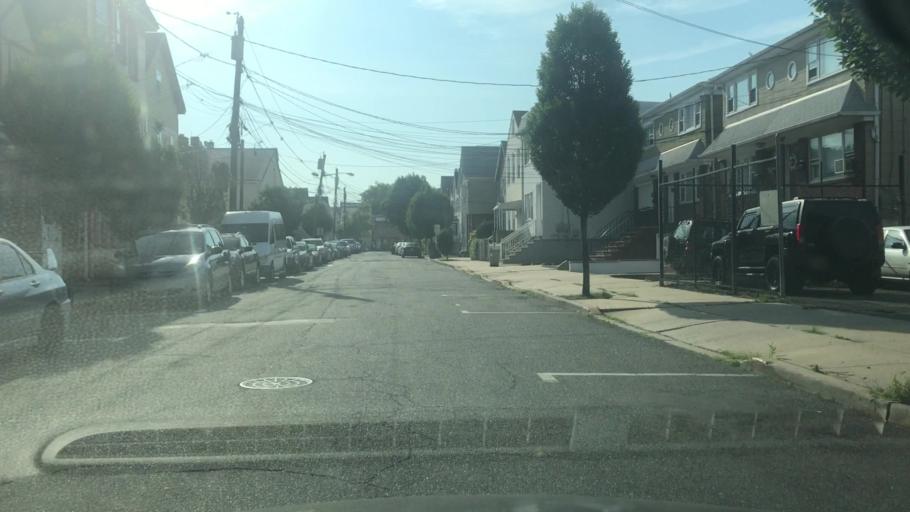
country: US
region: New Jersey
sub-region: Hudson County
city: East Newark
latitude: 40.7494
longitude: -74.1640
